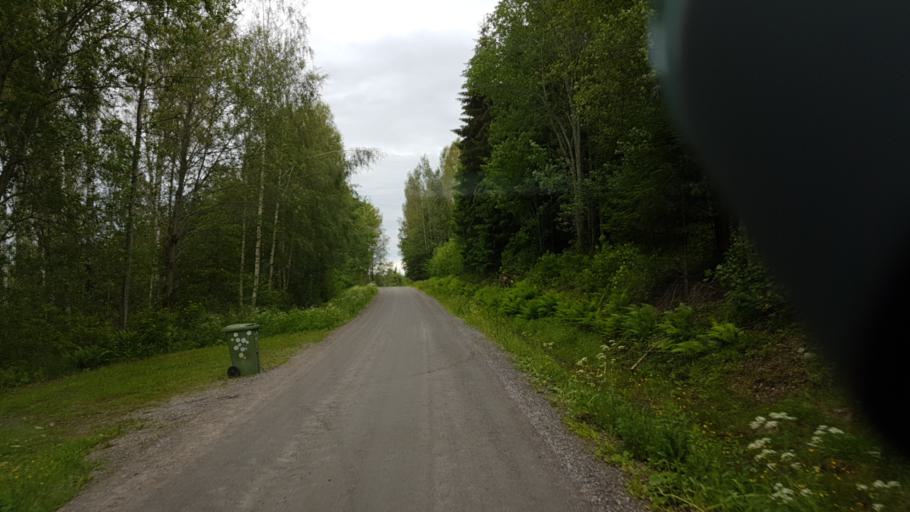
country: SE
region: Vaermland
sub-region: Eda Kommun
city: Amotfors
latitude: 59.7381
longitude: 12.2780
